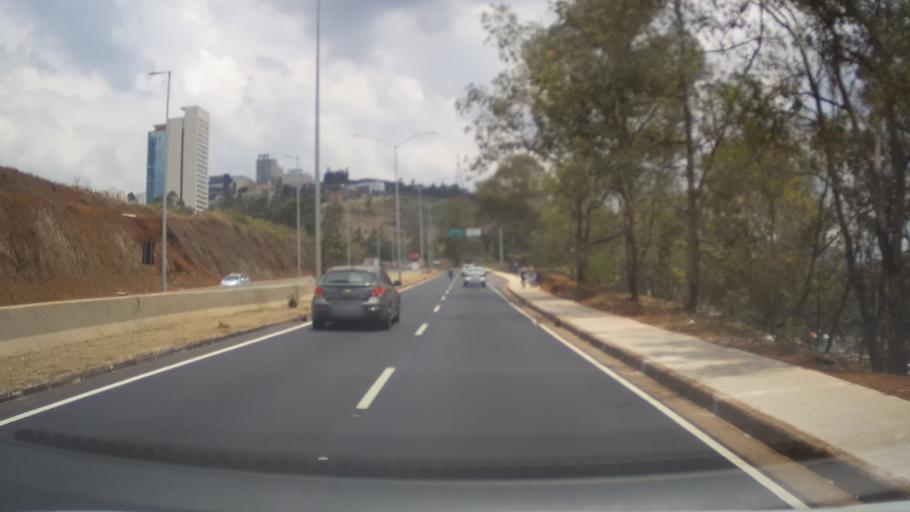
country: BR
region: Minas Gerais
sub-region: Belo Horizonte
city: Belo Horizonte
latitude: -19.9791
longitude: -43.9479
